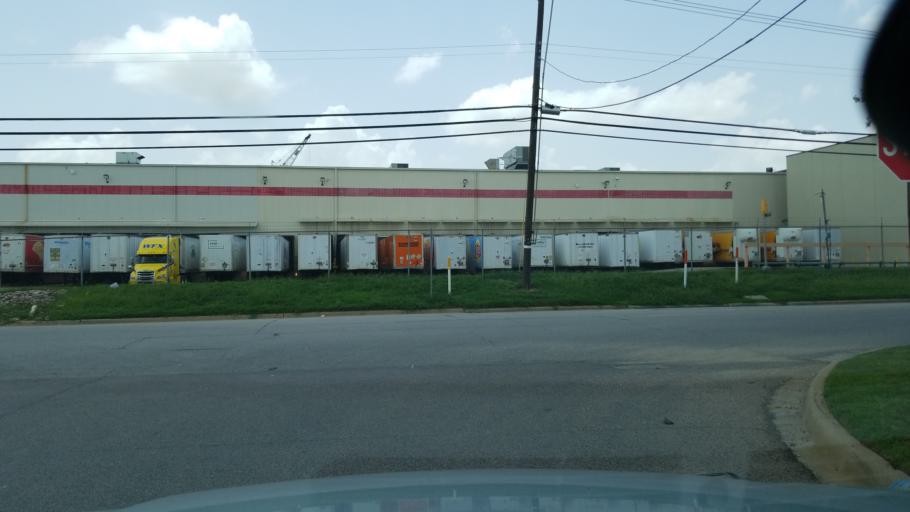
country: US
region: Texas
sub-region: Dallas County
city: Irving
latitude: 32.8211
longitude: -96.9167
